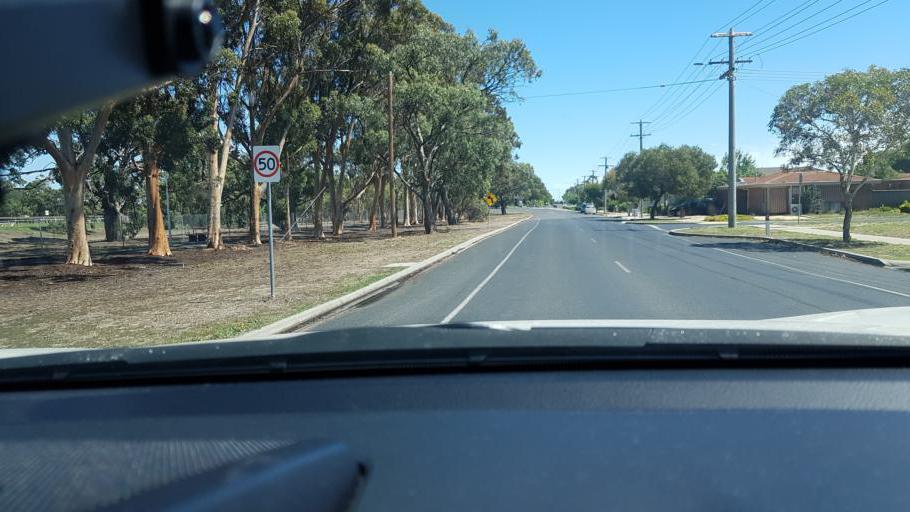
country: AU
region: Victoria
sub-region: Horsham
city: Horsham
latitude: -36.7118
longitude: 142.1900
